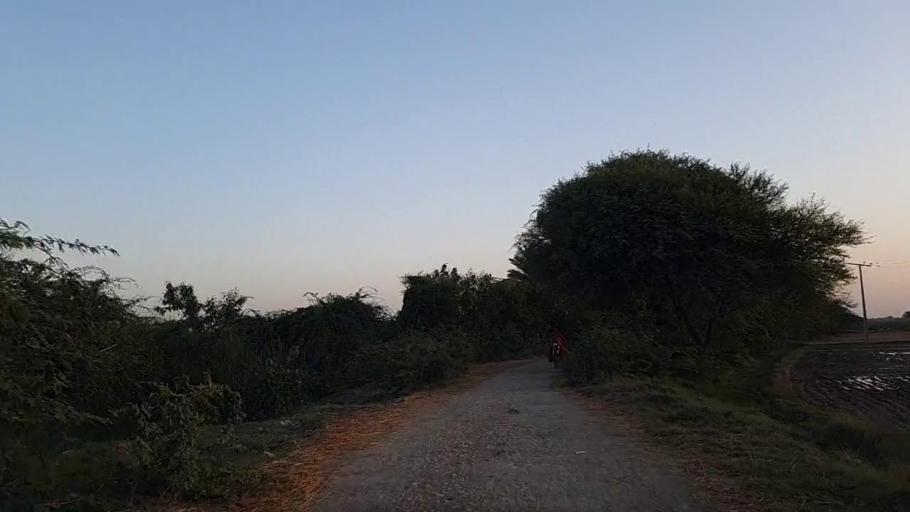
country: PK
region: Sindh
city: Mirpur Batoro
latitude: 24.6423
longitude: 68.1896
